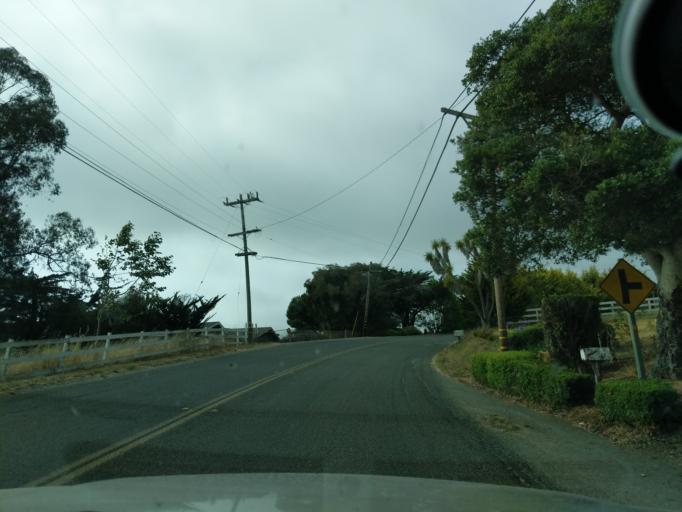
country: US
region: California
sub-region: Monterey County
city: Elkhorn
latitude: 36.8063
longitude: -121.7228
